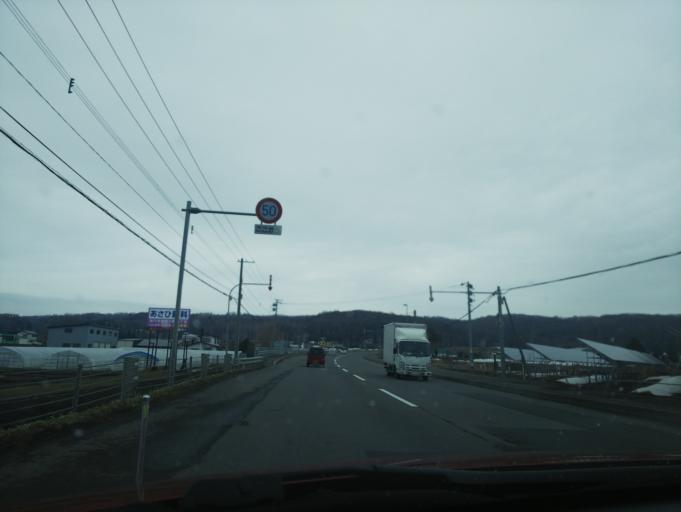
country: JP
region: Hokkaido
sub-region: Asahikawa-shi
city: Asahikawa
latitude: 43.8456
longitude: 142.4448
